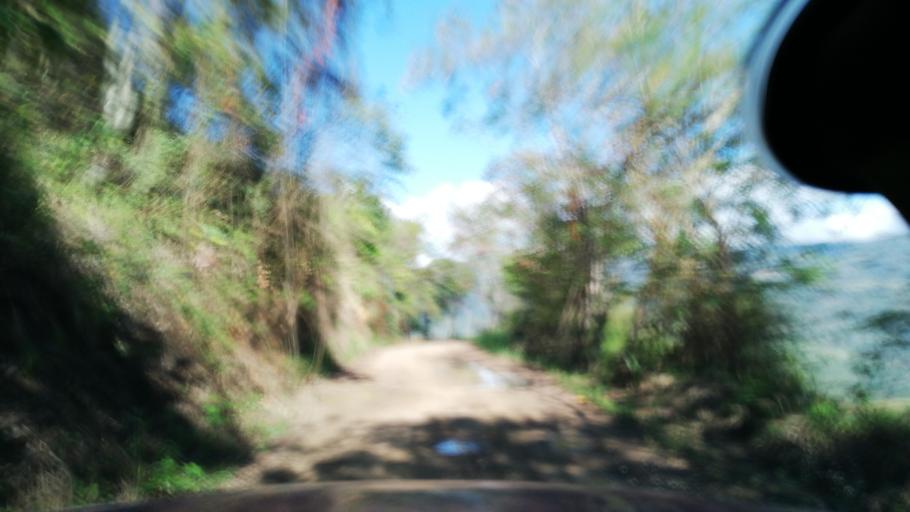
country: CO
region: Cundinamarca
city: Quipile
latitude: 4.7681
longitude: -74.6147
